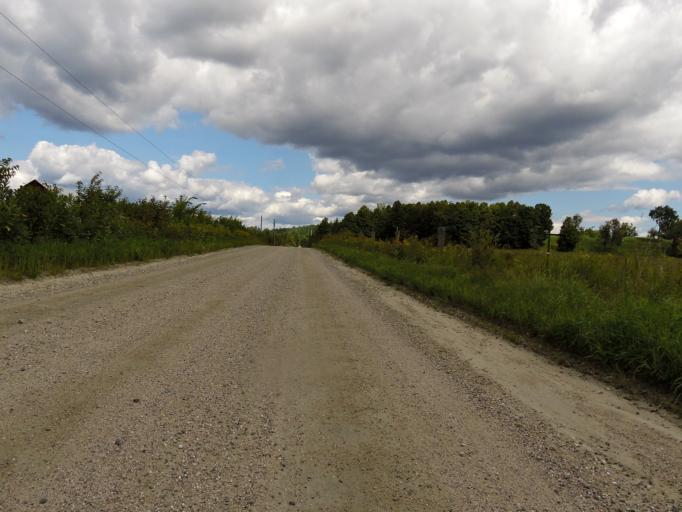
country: CA
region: Quebec
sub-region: Outaouais
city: Wakefield
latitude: 45.7892
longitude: -76.0274
